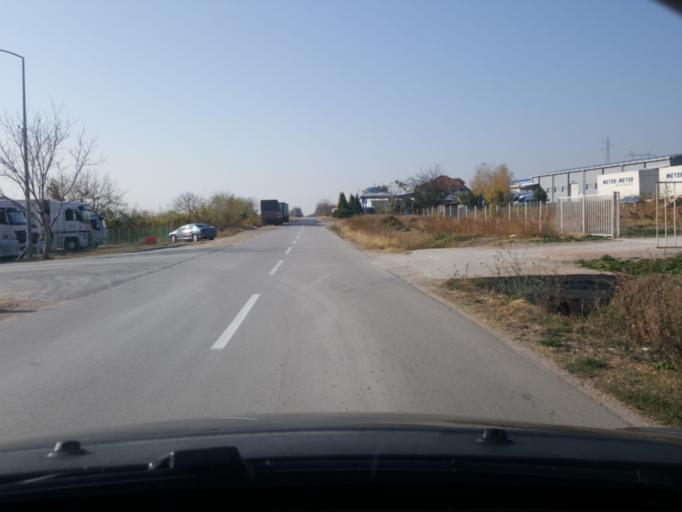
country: RS
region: Central Serbia
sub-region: Nisavski Okrug
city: Niska Banja
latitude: 43.3191
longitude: 22.0158
